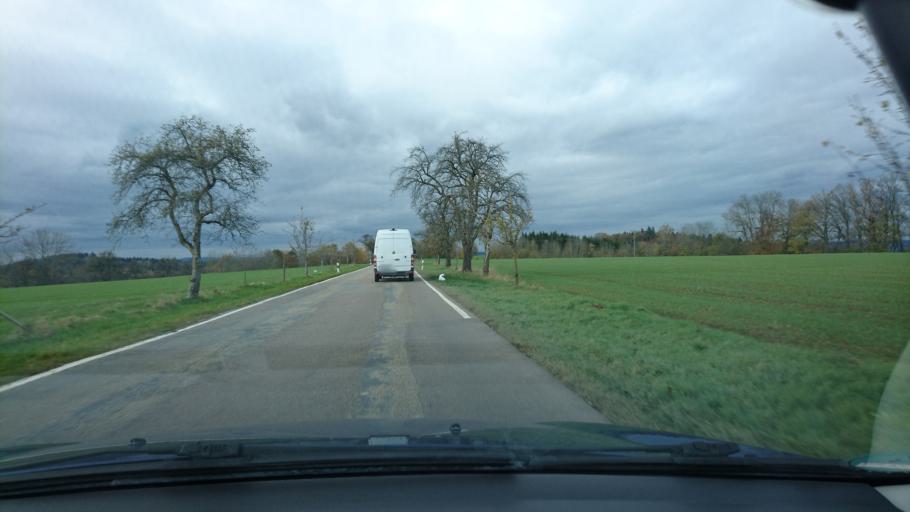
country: DE
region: Baden-Wuerttemberg
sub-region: Regierungsbezirk Stuttgart
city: Gschwend
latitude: 48.9319
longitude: 9.7934
